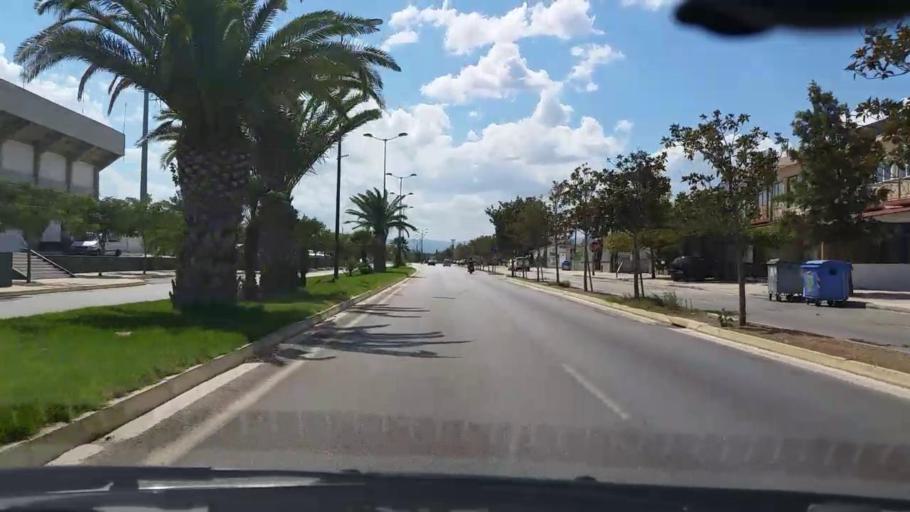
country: GR
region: Peloponnese
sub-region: Nomos Korinthias
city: Loutraki
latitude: 37.9662
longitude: 22.9783
